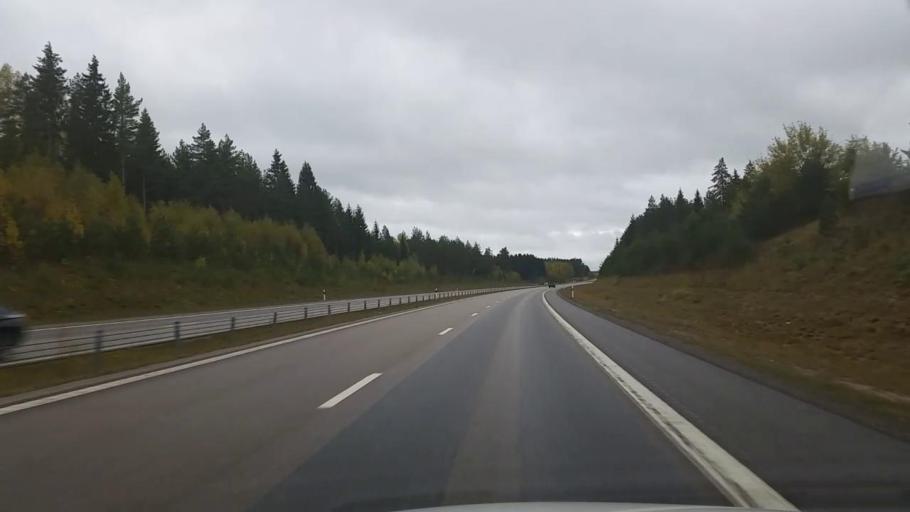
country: SE
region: Uppsala
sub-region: Osthammars Kommun
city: Bjorklinge
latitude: 60.1216
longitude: 17.5471
